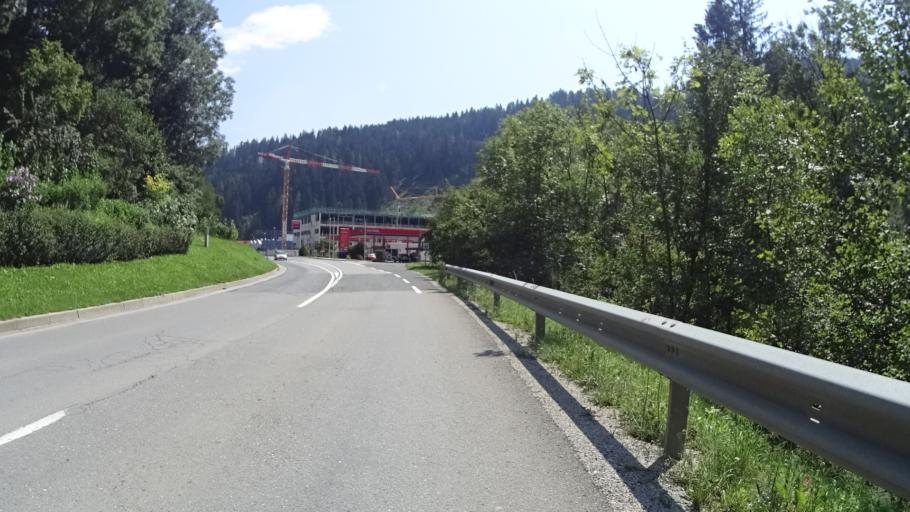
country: SI
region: Prevalje
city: Prevalje
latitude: 46.5437
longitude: 14.9031
